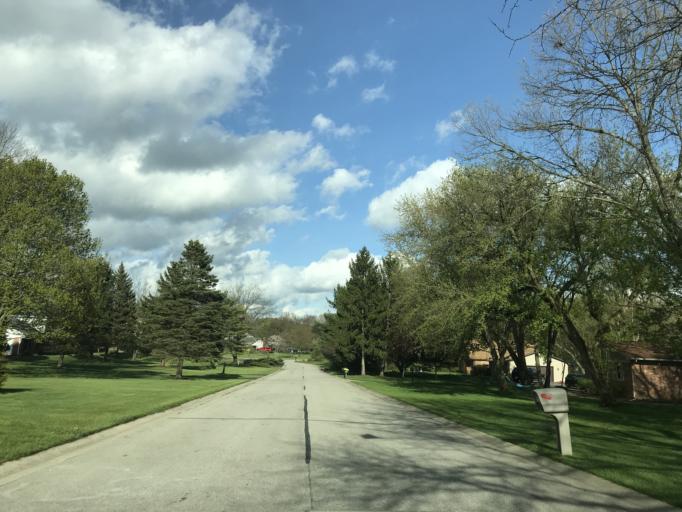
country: US
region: Michigan
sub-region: Livingston County
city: Brighton
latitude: 42.5286
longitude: -83.7187
